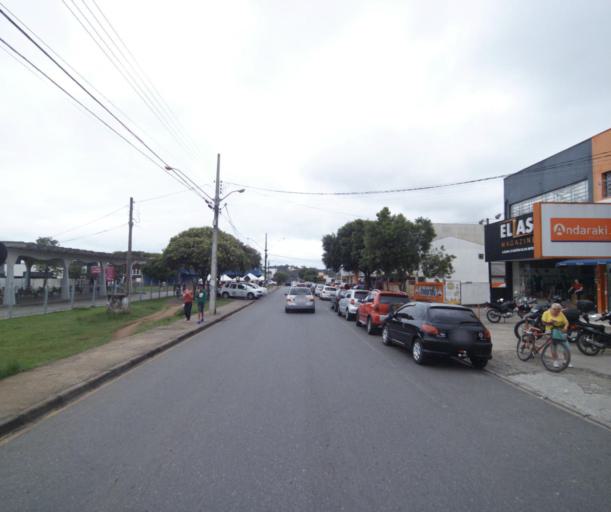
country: BR
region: Parana
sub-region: Quatro Barras
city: Quatro Barras
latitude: -25.3632
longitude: -49.1012
